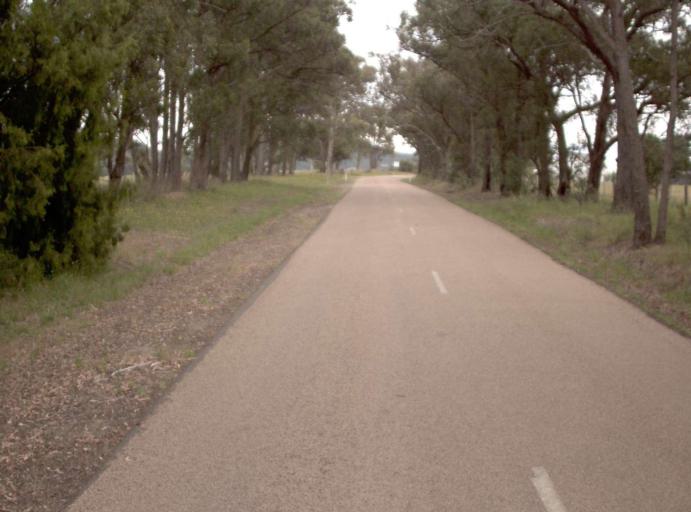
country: AU
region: Victoria
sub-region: East Gippsland
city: Bairnsdale
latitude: -37.7407
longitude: 147.5980
